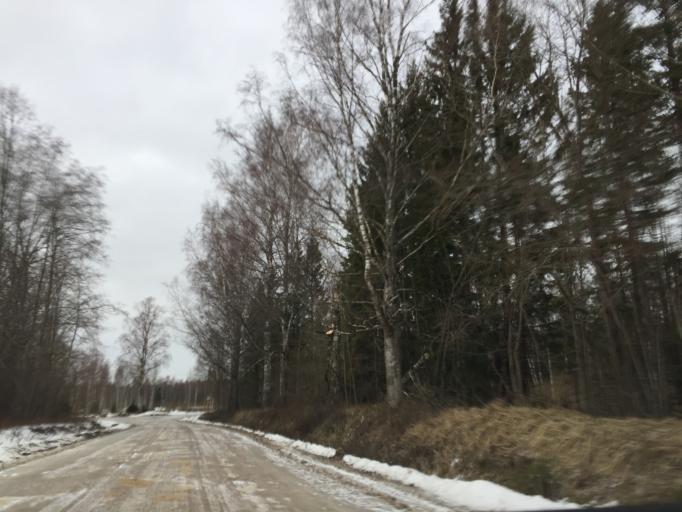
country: LV
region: Salacgrivas
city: Salacgriva
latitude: 57.6526
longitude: 24.4600
